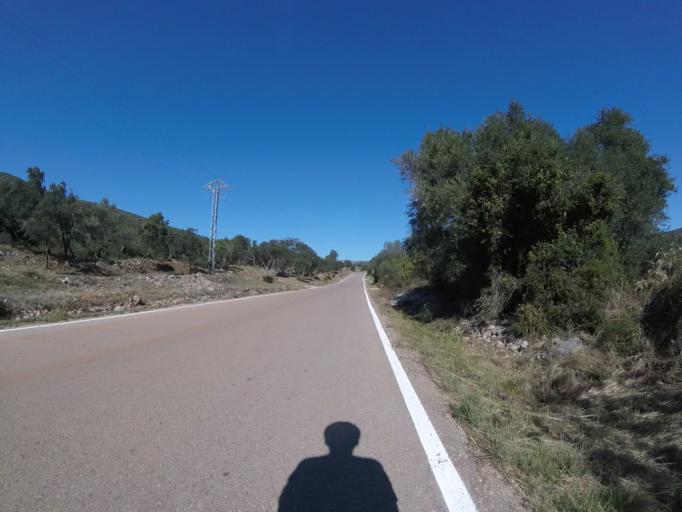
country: ES
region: Valencia
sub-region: Provincia de Castello
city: Santa Magdalena de Pulpis
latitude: 40.3658
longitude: 0.2769
